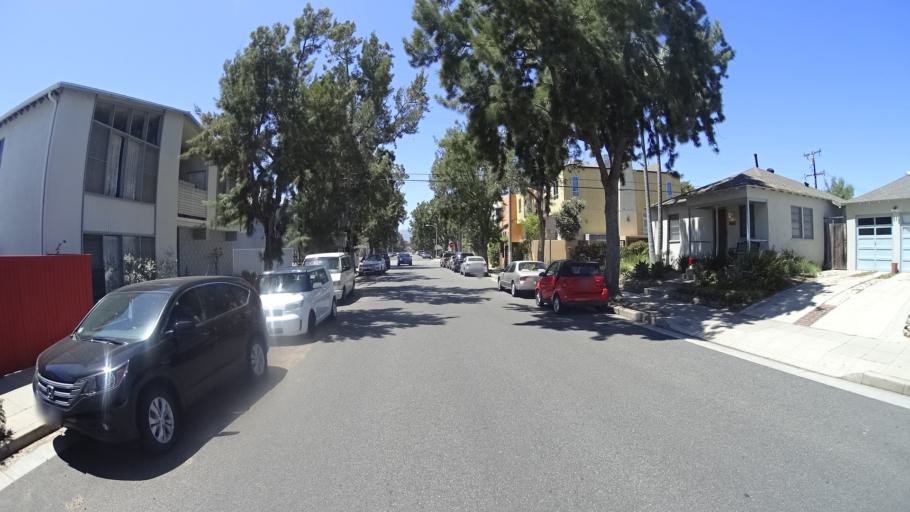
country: US
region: California
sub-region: Los Angeles County
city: Santa Monica
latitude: 34.0099
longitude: -118.4777
